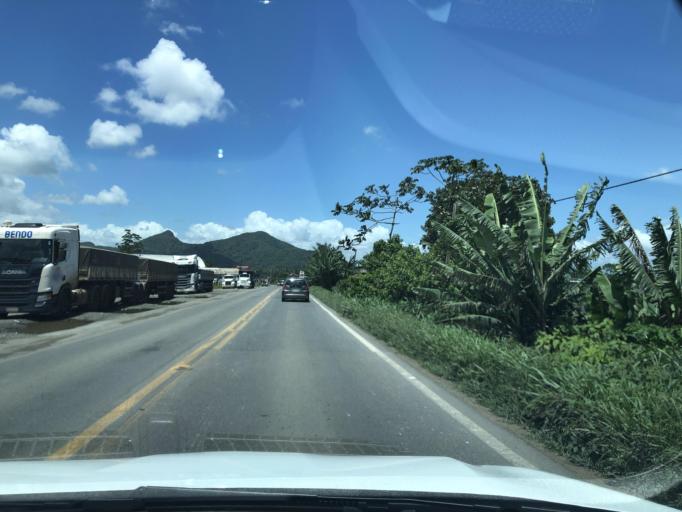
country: BR
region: Santa Catarina
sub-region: Sao Francisco Do Sul
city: Sao Francisco do Sul
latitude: -26.2682
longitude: -48.6374
